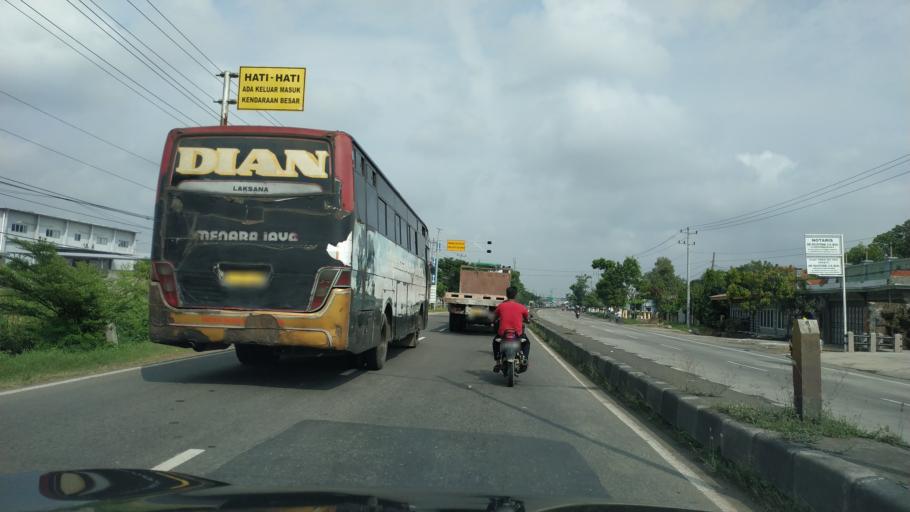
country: ID
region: Central Java
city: Bulakamba
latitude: -6.8750
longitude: 108.9302
